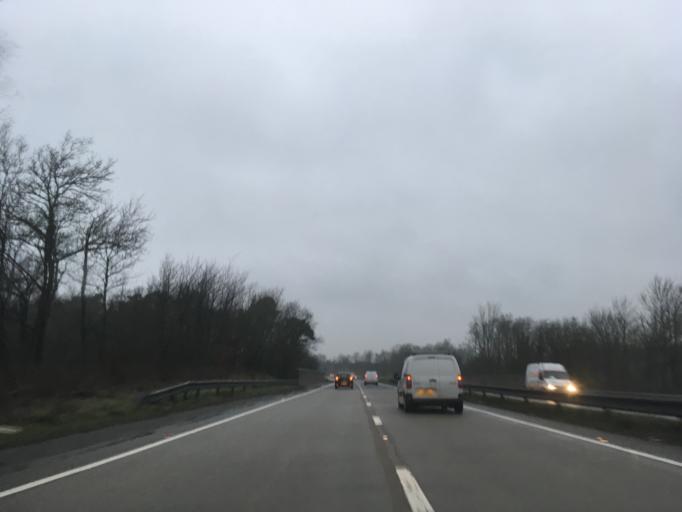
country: GB
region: Wales
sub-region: Cardiff
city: Radyr
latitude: 51.4797
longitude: -3.2818
